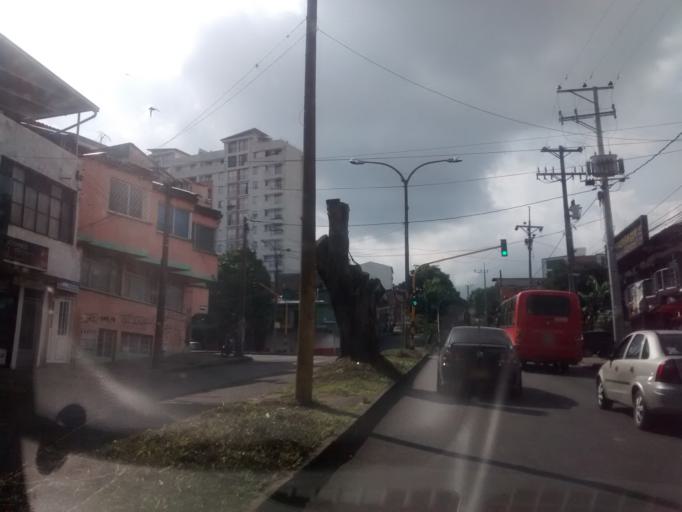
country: CO
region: Tolima
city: Ibague
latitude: 4.4463
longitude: -75.2353
